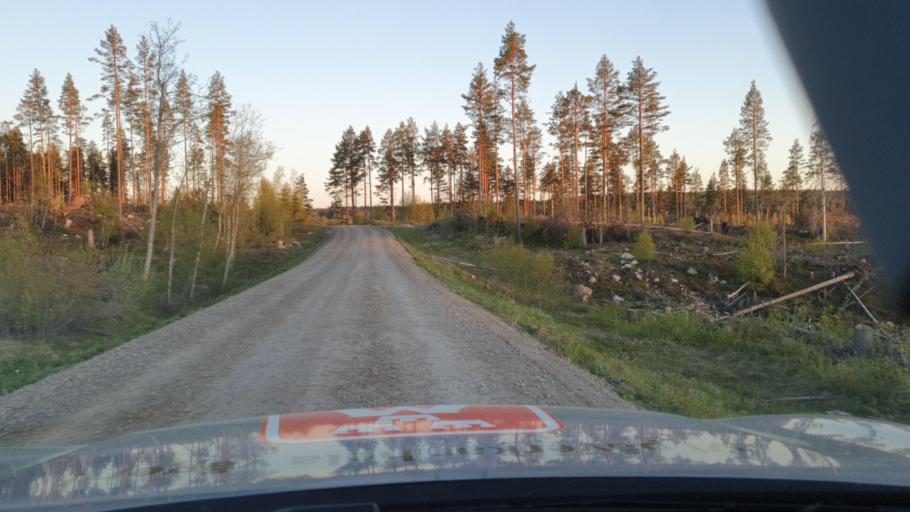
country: SE
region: Vaesternorrland
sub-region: OErnskoeldsviks Kommun
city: Bjasta
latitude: 63.5099
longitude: 18.4921
